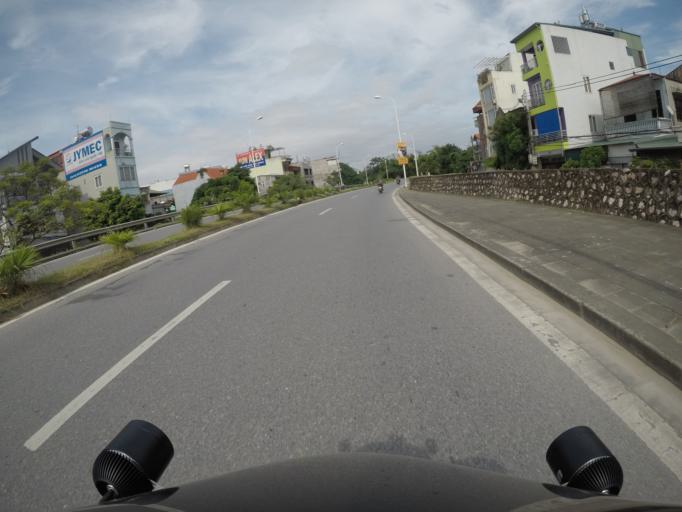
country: VN
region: Ha Noi
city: Tay Ho
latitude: 21.0890
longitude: 105.8135
